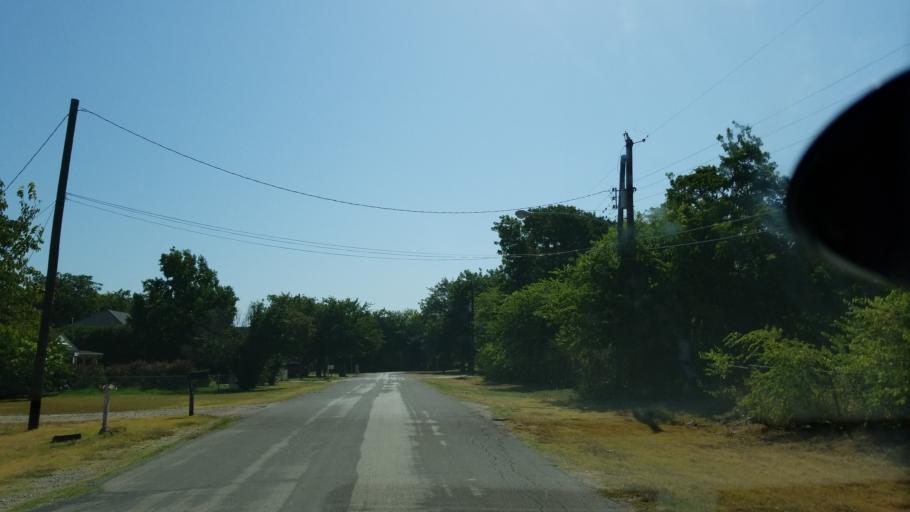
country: US
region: Texas
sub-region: Dallas County
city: Cockrell Hill
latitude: 32.7014
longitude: -96.9209
